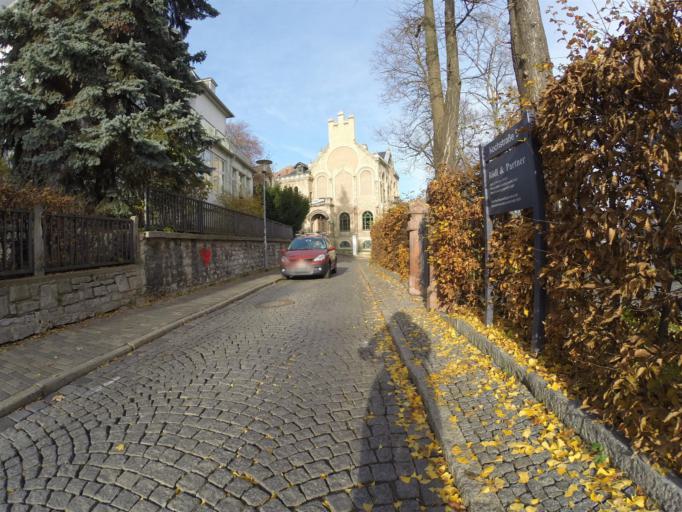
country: DE
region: Thuringia
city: Jena
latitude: 50.9260
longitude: 11.5790
